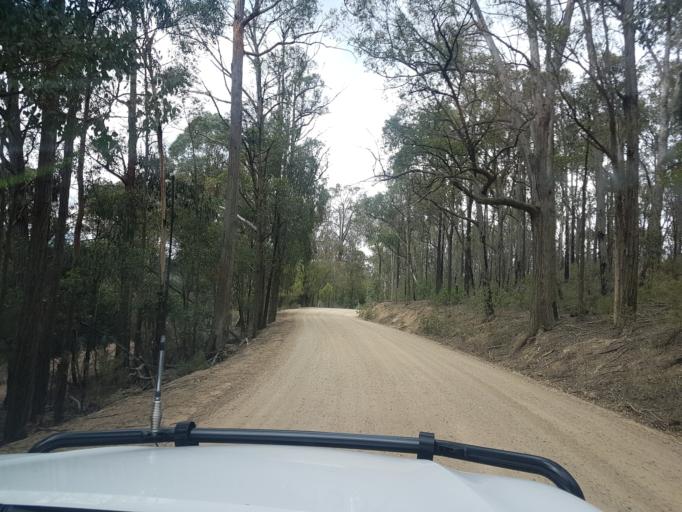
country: AU
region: Victoria
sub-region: East Gippsland
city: Bairnsdale
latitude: -37.6965
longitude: 147.5716
